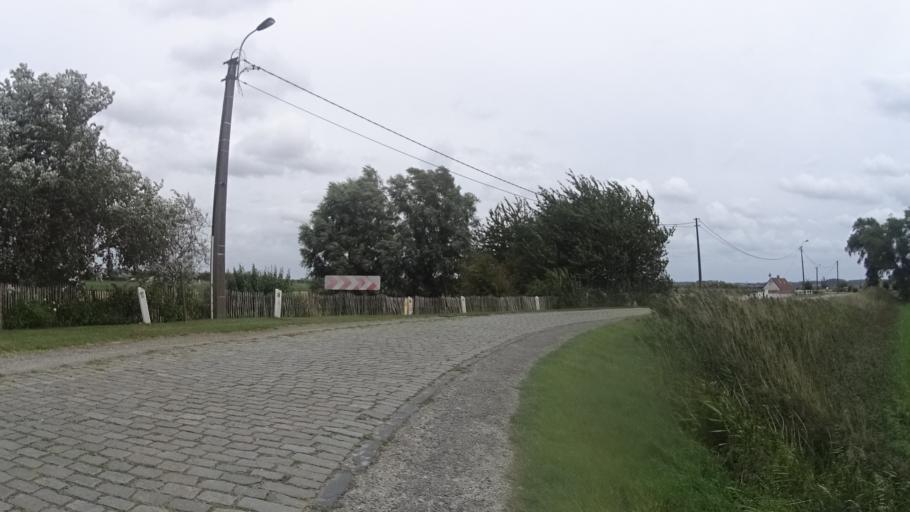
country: NL
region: Zeeland
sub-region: Gemeente Sluis
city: Sluis
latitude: 51.3373
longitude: 3.3485
